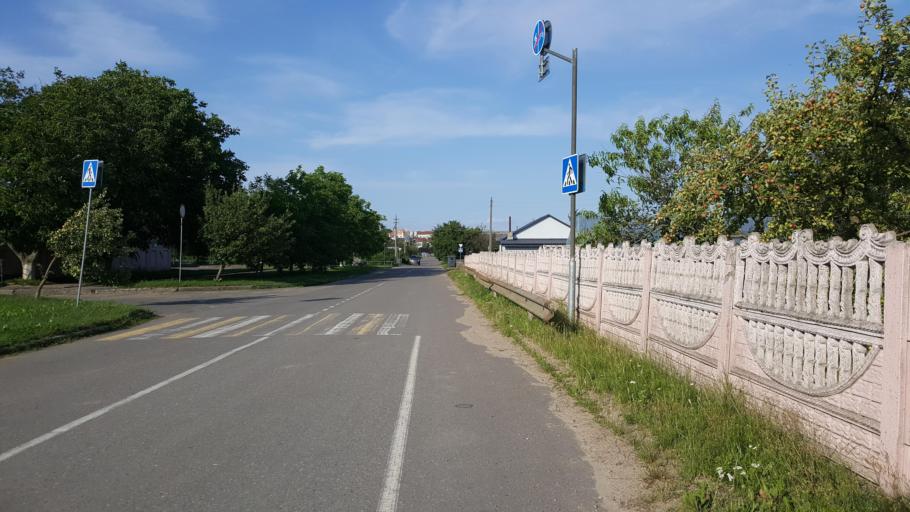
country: BY
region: Brest
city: Vysokaye
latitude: 52.3755
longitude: 23.3605
